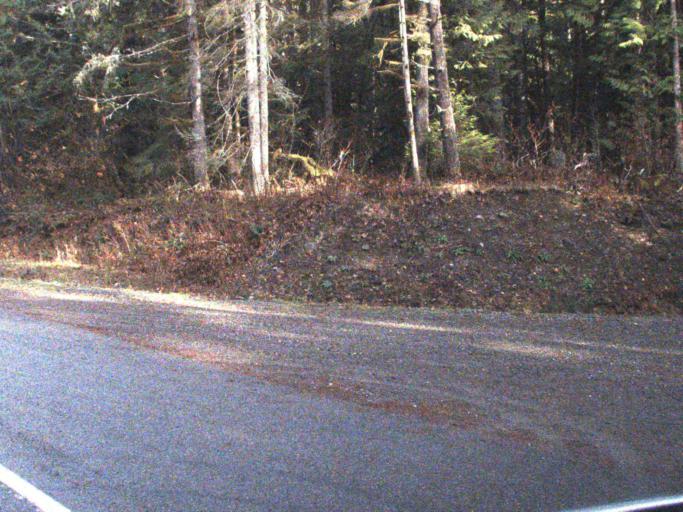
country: US
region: Washington
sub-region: Whatcom County
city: Peaceful Valley
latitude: 48.9032
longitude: -121.9116
